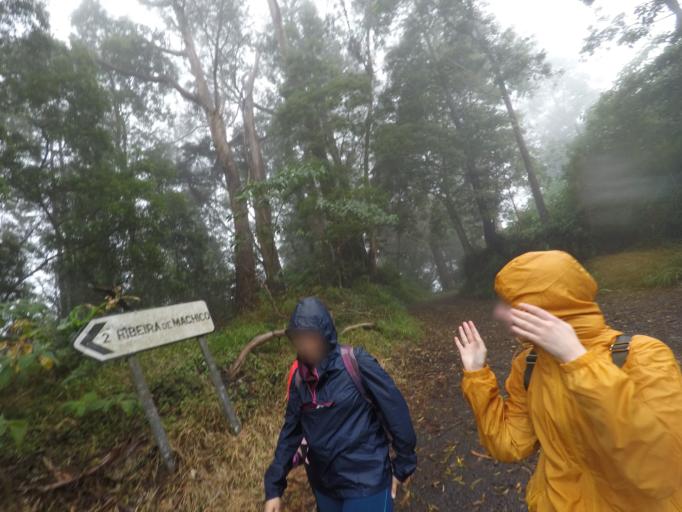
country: PT
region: Madeira
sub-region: Santa Cruz
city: Santa Cruz
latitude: 32.7468
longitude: -16.8243
